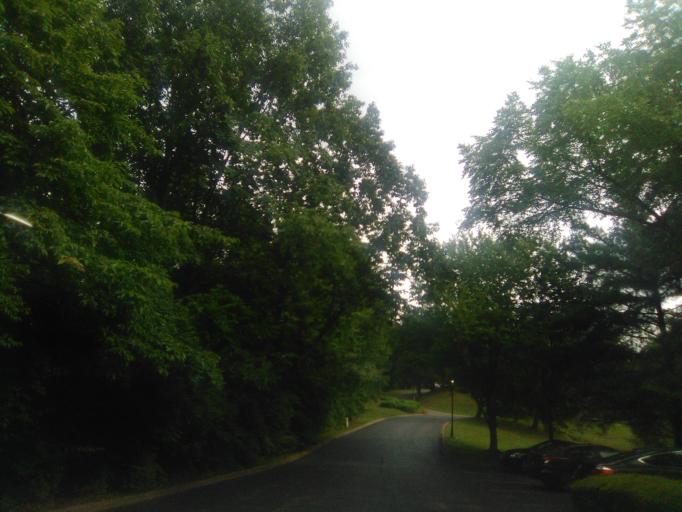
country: US
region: Tennessee
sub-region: Davidson County
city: Belle Meade
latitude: 36.0815
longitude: -86.9030
